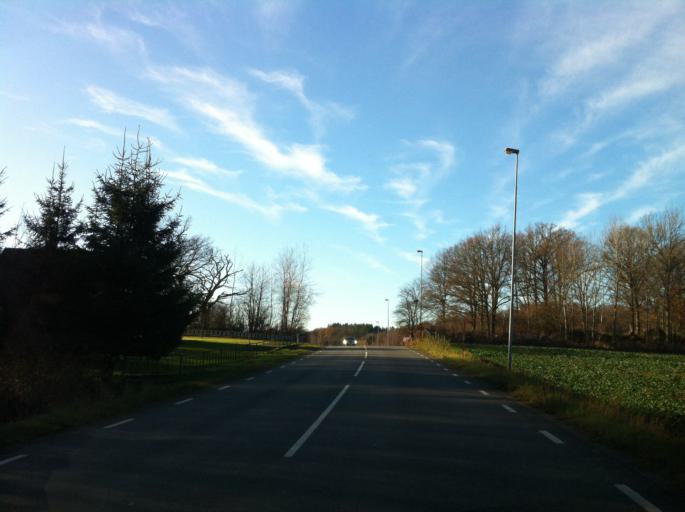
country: SE
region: Blekinge
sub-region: Karlshamns Kommun
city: Karlshamn
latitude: 56.1994
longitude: 14.9437
